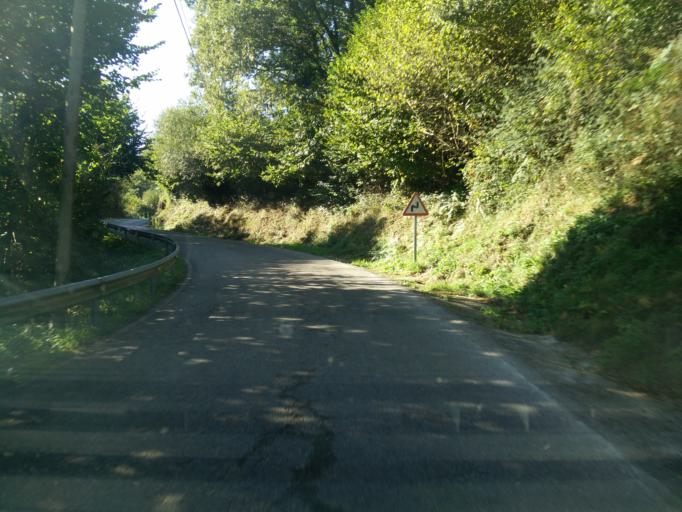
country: ES
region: Cantabria
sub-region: Provincia de Cantabria
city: Vega de Pas
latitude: 43.1554
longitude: -3.8218
